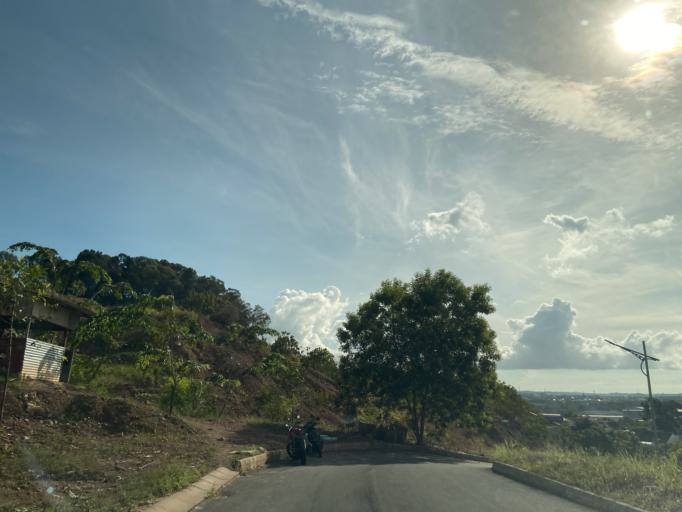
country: SG
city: Singapore
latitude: 1.0968
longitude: 104.0275
